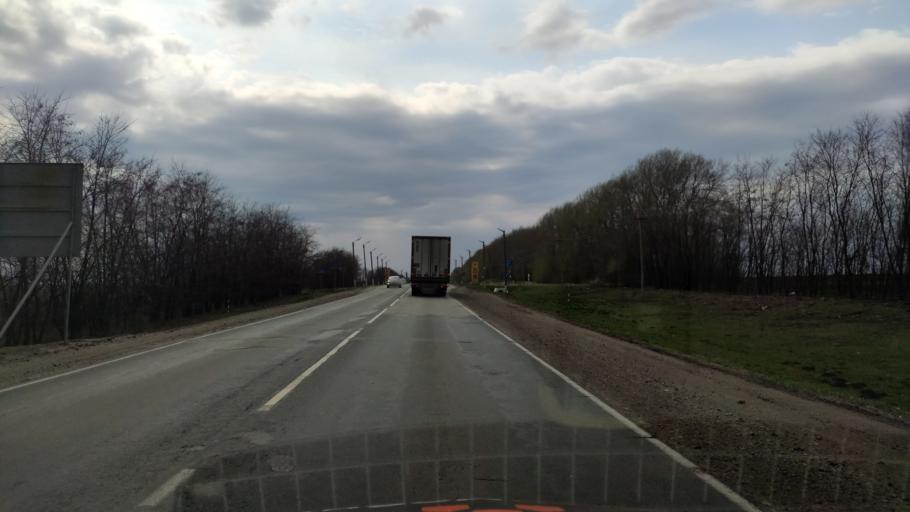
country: RU
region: Voronezj
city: Nizhnedevitsk
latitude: 51.5629
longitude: 38.2576
